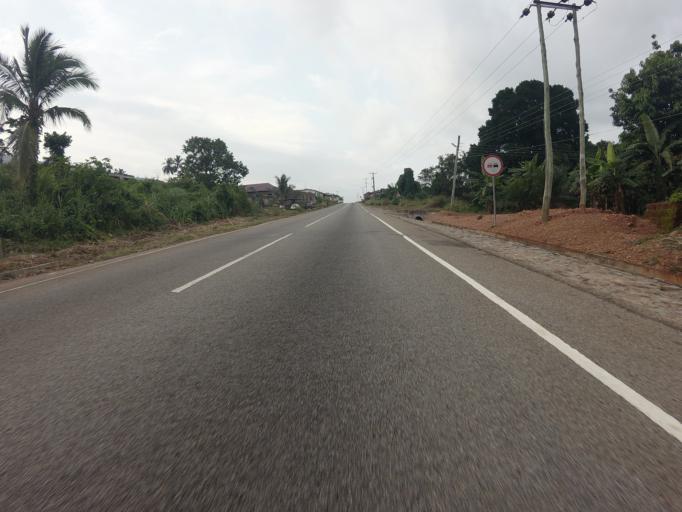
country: GH
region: Volta
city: Ho
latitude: 6.6568
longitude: 0.4709
